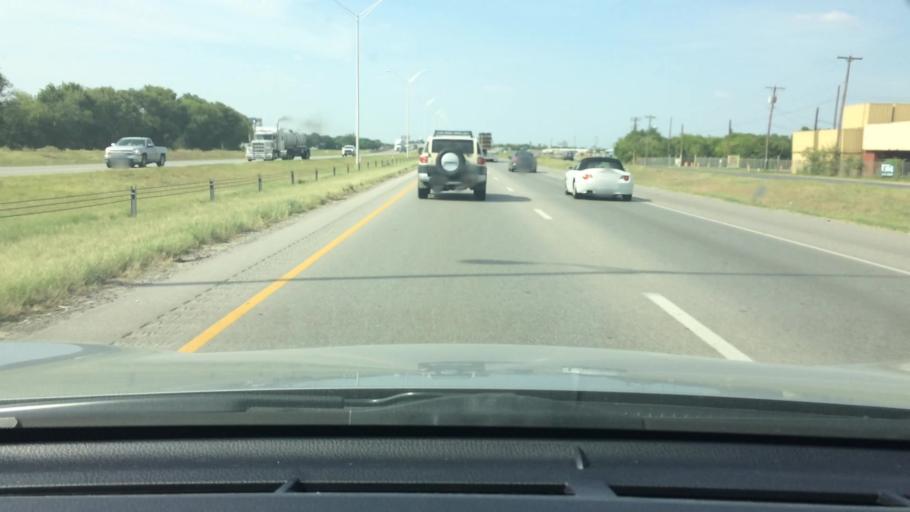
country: US
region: Texas
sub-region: Bexar County
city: China Grove
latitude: 29.3819
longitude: -98.3917
